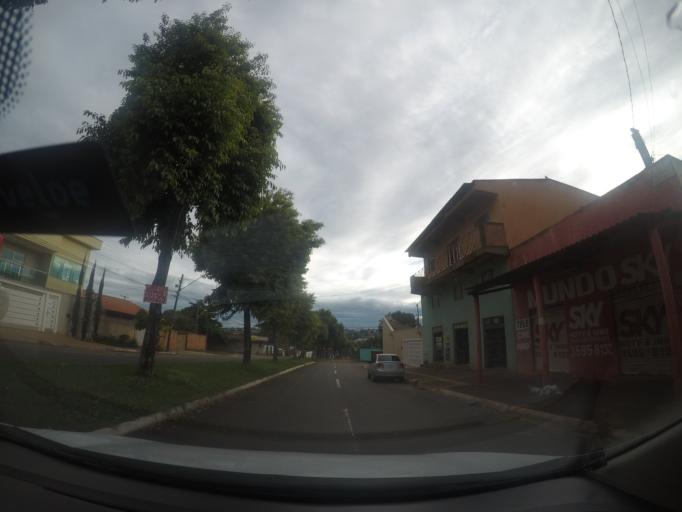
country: BR
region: Goias
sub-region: Goiania
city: Goiania
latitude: -16.6148
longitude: -49.3406
